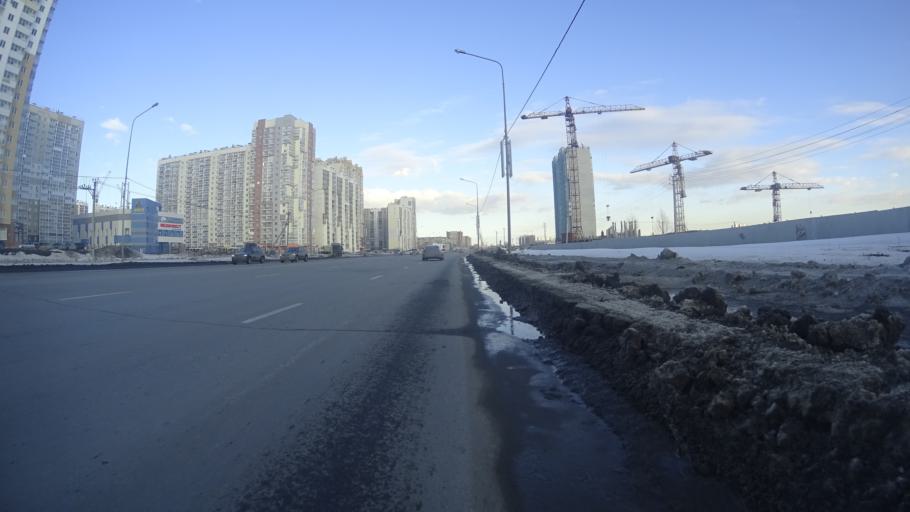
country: RU
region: Chelyabinsk
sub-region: Gorod Chelyabinsk
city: Chelyabinsk
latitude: 55.1743
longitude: 61.3235
